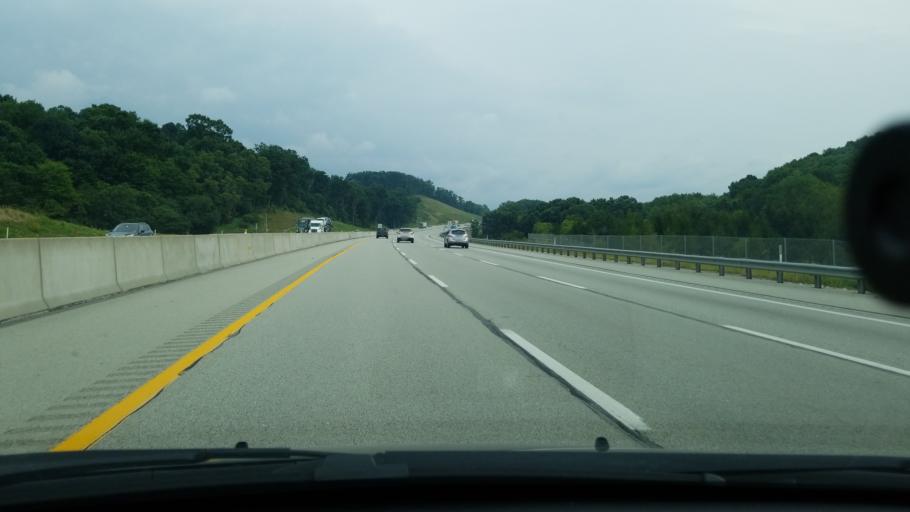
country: US
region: Pennsylvania
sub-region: Allegheny County
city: Gibsonia
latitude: 40.6295
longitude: -79.9850
